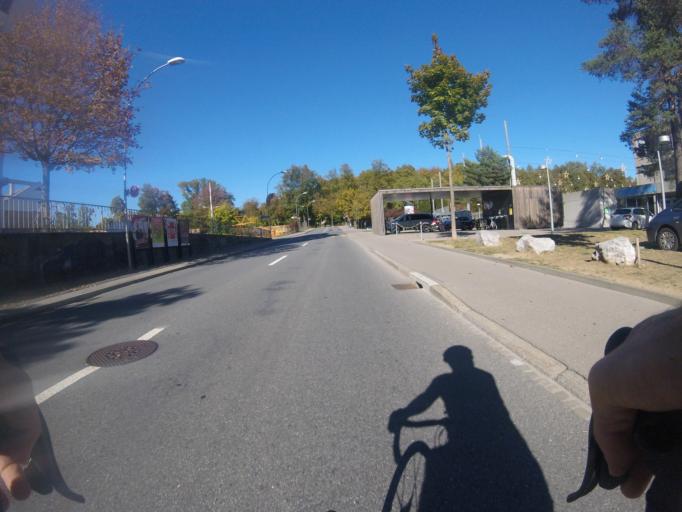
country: CH
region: Bern
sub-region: Bern-Mittelland District
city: Koniz
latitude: 46.9484
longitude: 7.4034
